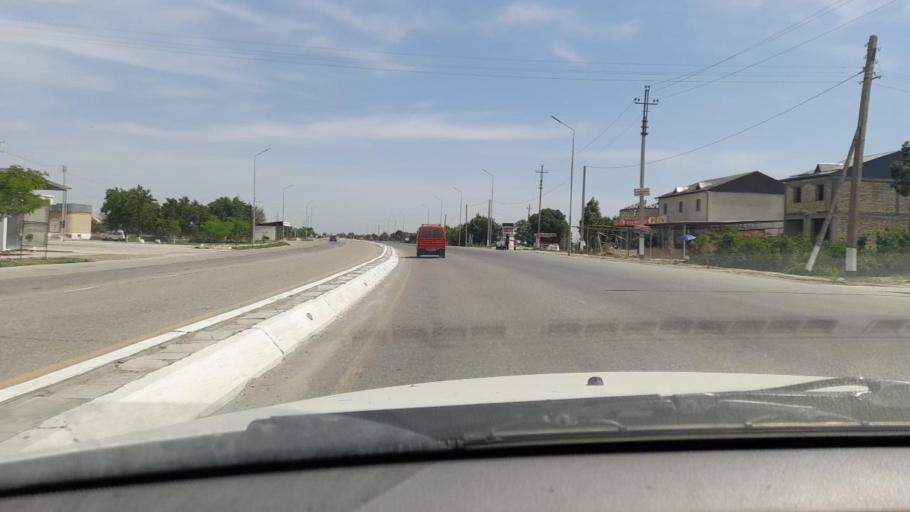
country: UZ
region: Bukhara
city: Galaosiyo
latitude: 39.8658
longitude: 64.4492
